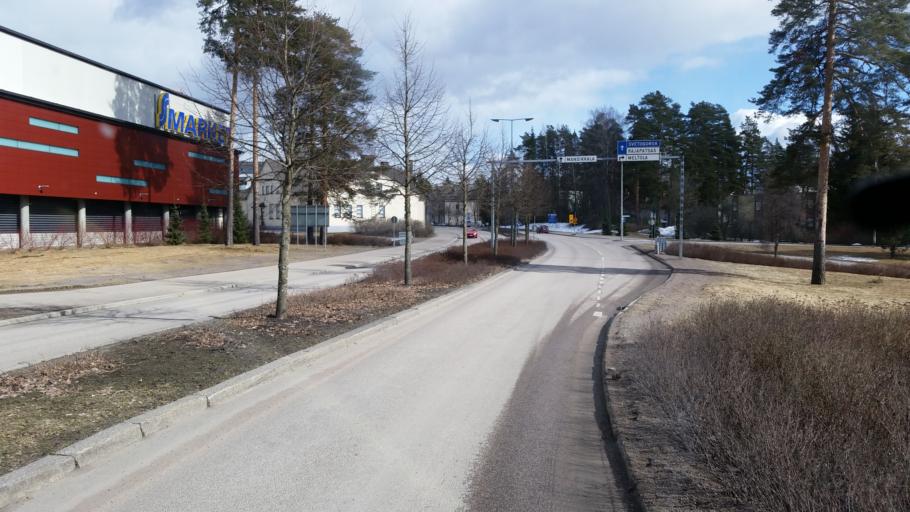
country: FI
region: South Karelia
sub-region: Imatra
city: Imatra
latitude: 61.1695
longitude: 28.7648
